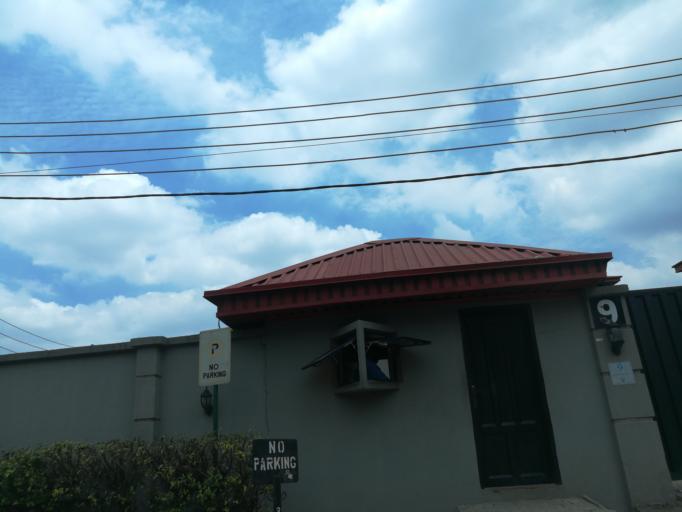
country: NG
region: Lagos
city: Ikeja
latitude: 6.5970
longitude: 3.3517
